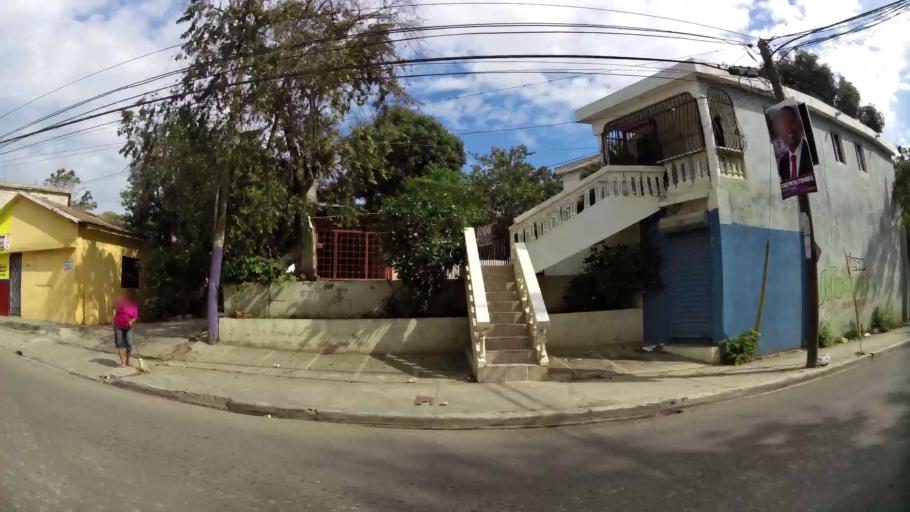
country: DO
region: Santiago
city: Santiago de los Caballeros
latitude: 19.4267
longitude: -70.7110
